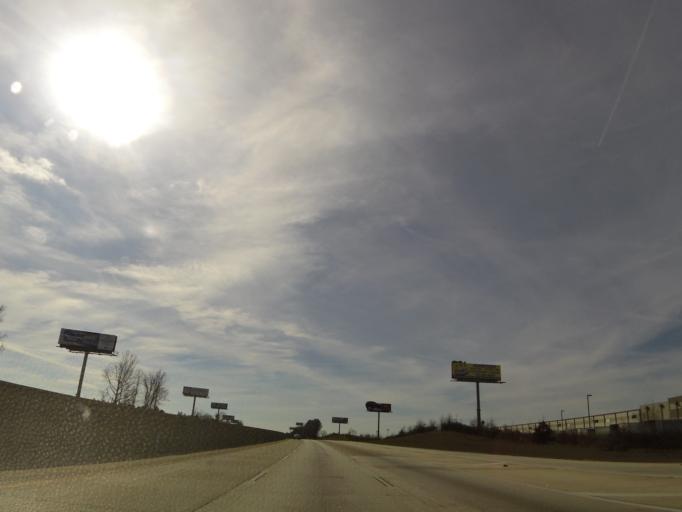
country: US
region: Georgia
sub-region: Fulton County
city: Fairburn
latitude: 33.5433
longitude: -84.5837
